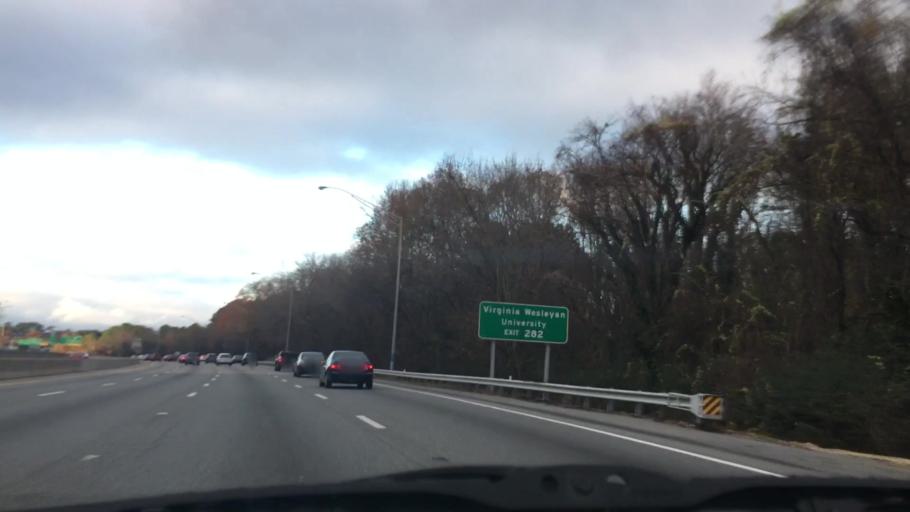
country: US
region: Virginia
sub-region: City of Norfolk
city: Norfolk
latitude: 36.8677
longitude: -76.1947
